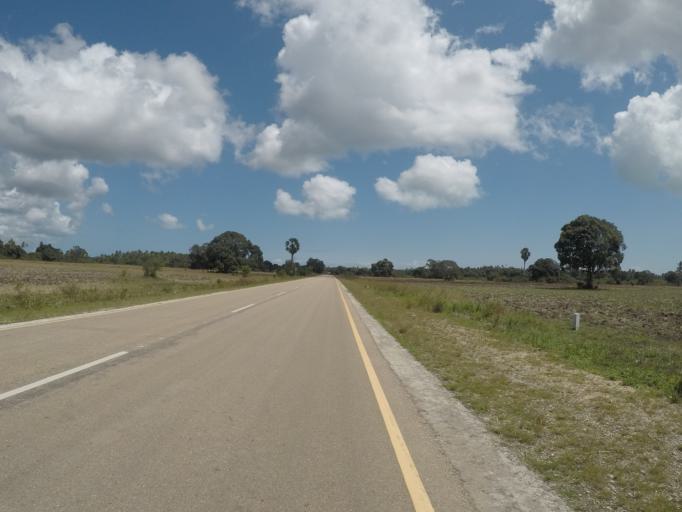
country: TZ
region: Zanzibar Central/South
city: Koani
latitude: -6.2243
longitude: 39.3616
